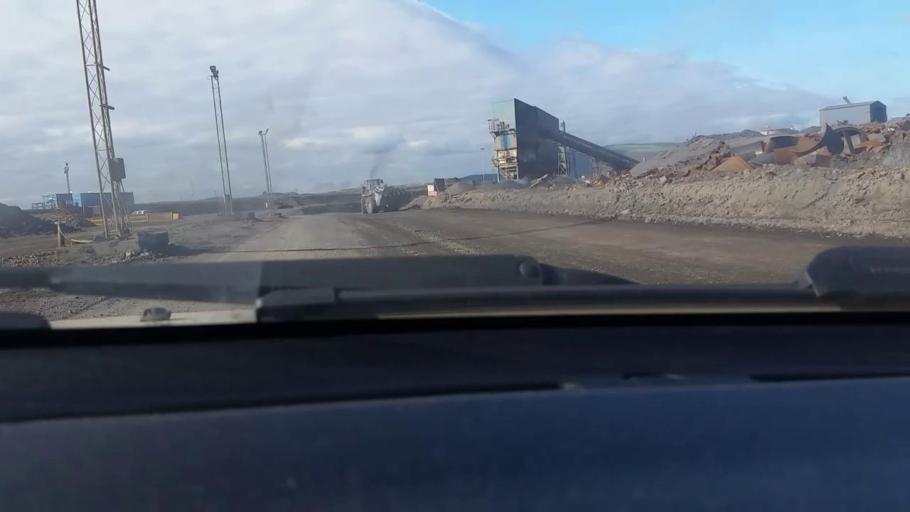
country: GB
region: Wales
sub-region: Neath Port Talbot
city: Taibach
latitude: 51.5644
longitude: -3.7801
